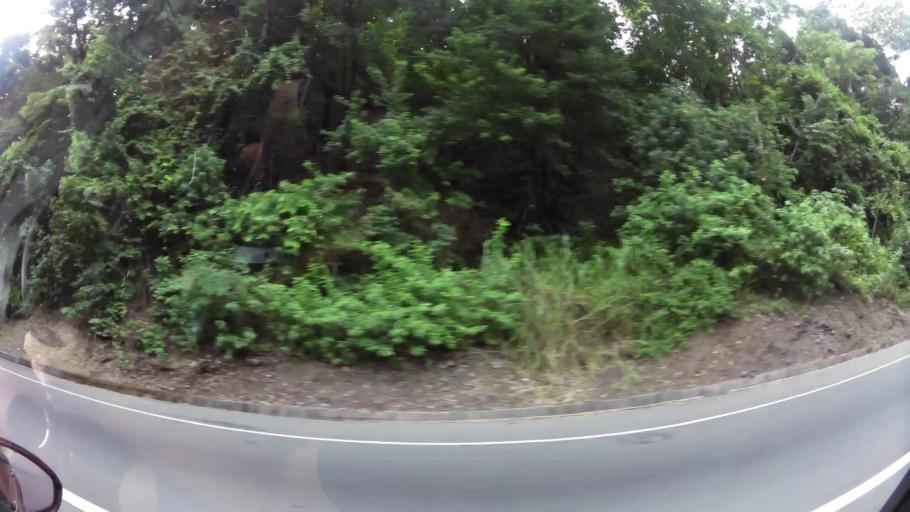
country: TT
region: San Juan/Laventille
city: Laventille
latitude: 10.6678
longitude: -61.4855
